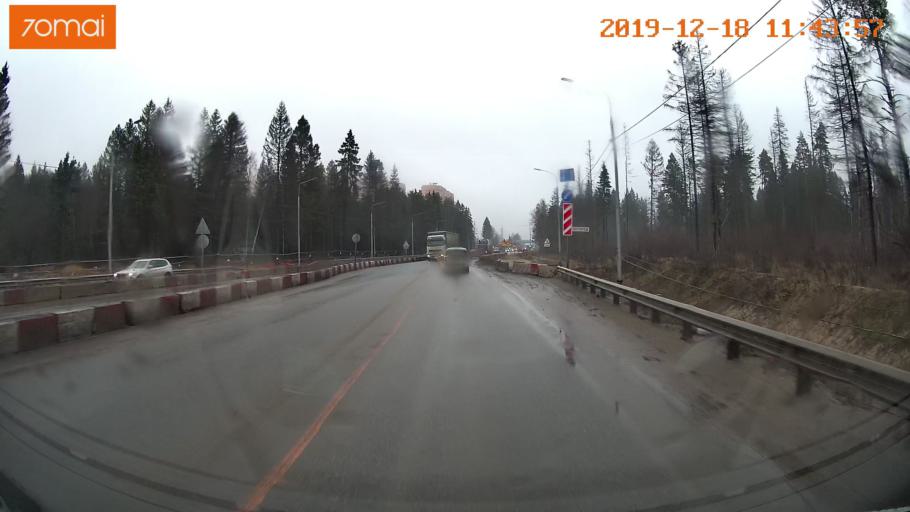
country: RU
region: Moskovskaya
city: Zvenigorod
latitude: 55.7394
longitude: 36.8781
